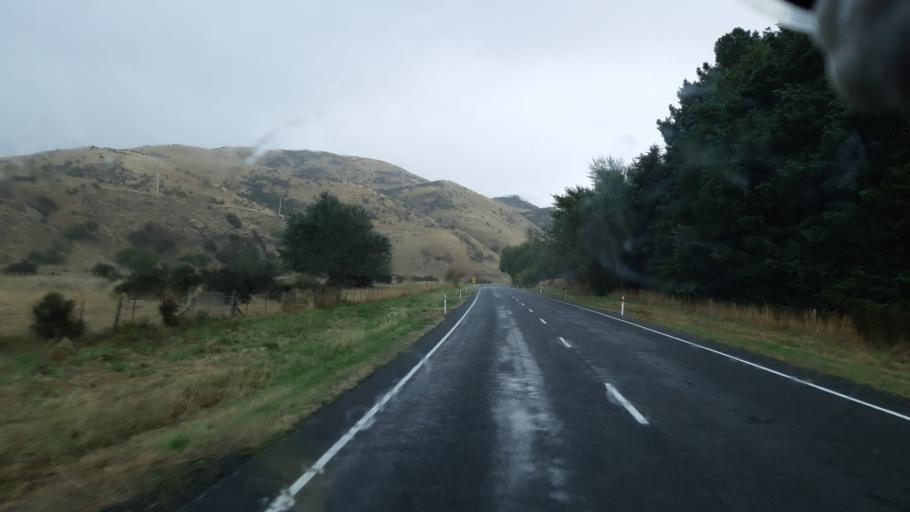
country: NZ
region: Canterbury
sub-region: Hurunui District
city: Amberley
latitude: -42.6876
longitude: 172.7943
